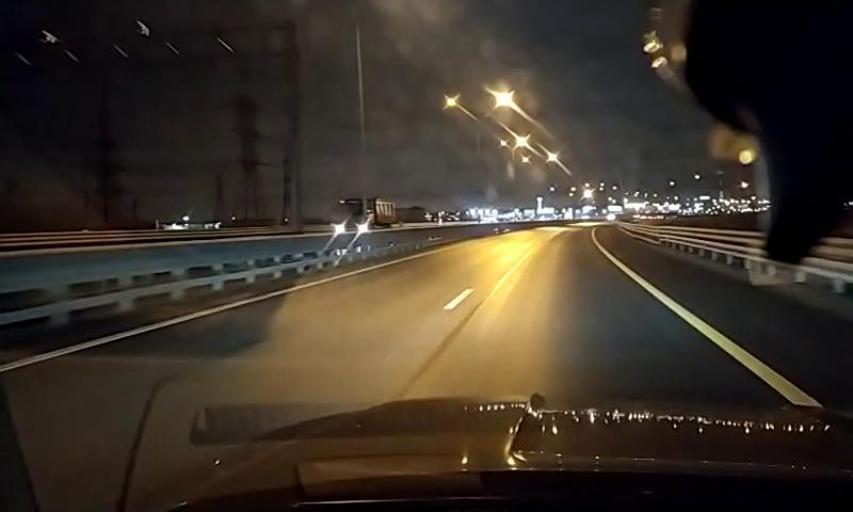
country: RU
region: Leningrad
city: Bugry
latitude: 60.1010
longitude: 30.3841
